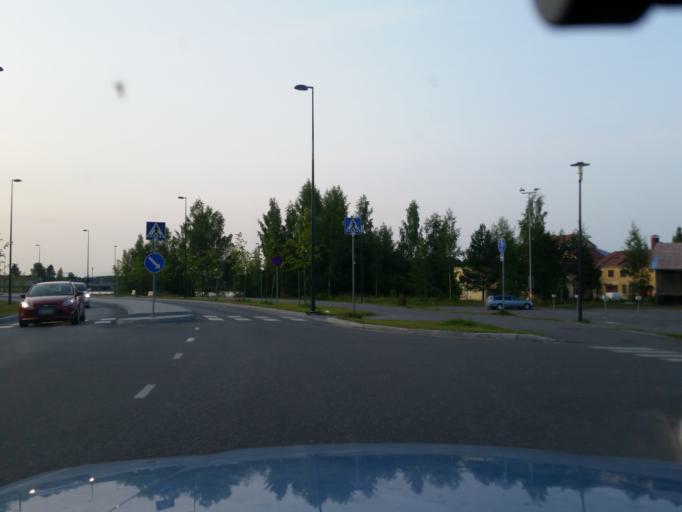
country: FI
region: Southern Savonia
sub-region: Savonlinna
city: Savonlinna
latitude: 61.8713
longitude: 28.8752
